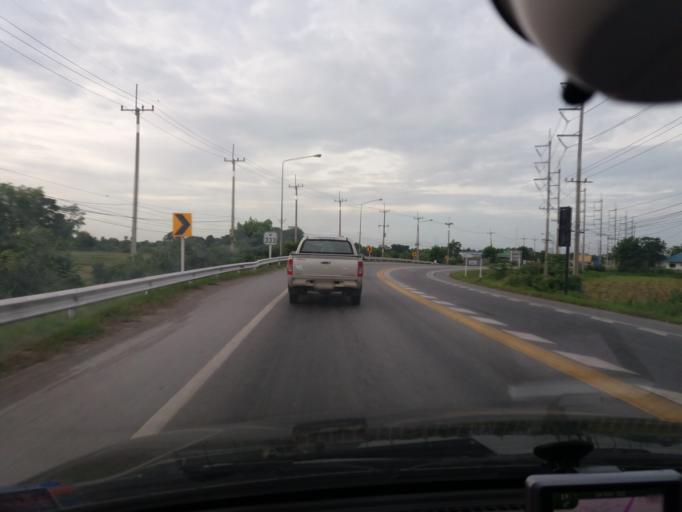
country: TH
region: Suphan Buri
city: U Thong
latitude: 14.5117
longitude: 99.9159
